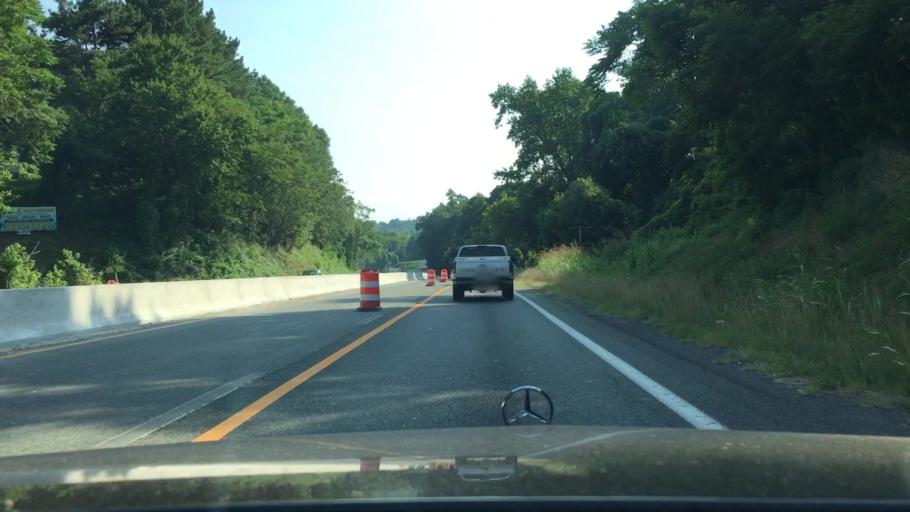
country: US
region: Virginia
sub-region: Amherst County
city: Madison Heights
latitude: 37.4171
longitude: -79.1275
